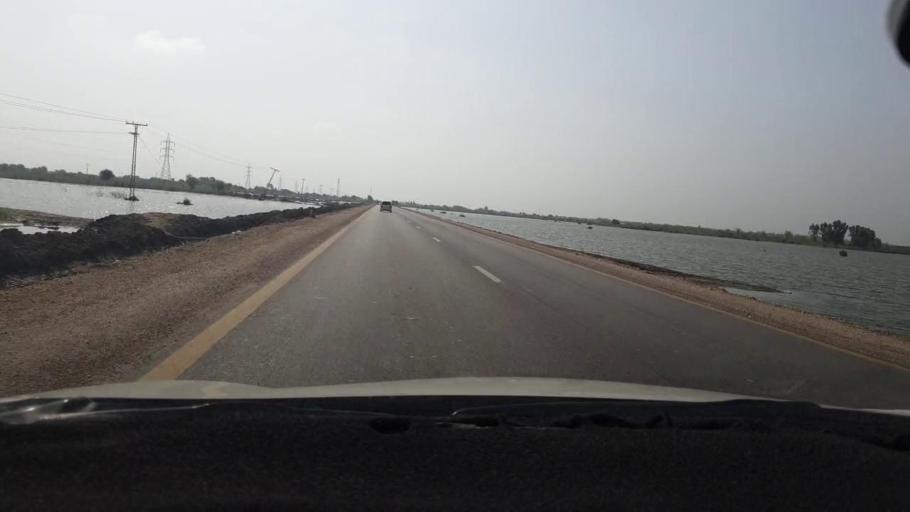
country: PK
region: Sindh
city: Jhol
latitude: 25.8967
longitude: 69.0256
